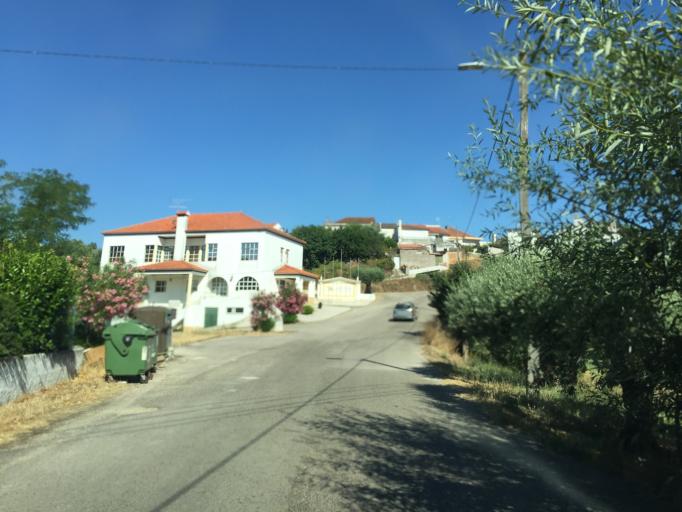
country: PT
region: Santarem
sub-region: Tomar
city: Tomar
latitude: 39.6079
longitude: -8.3321
